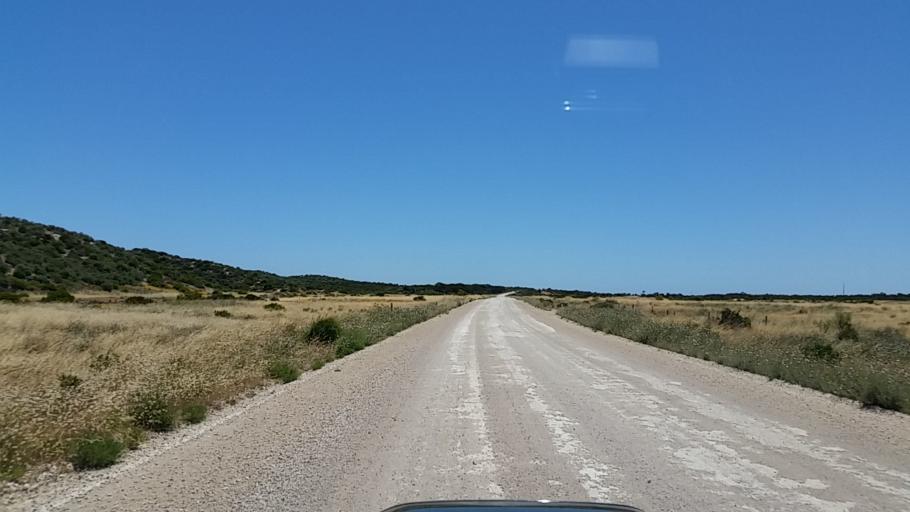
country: AU
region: South Australia
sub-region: Yorke Peninsula
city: Honiton
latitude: -35.2211
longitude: 137.0618
